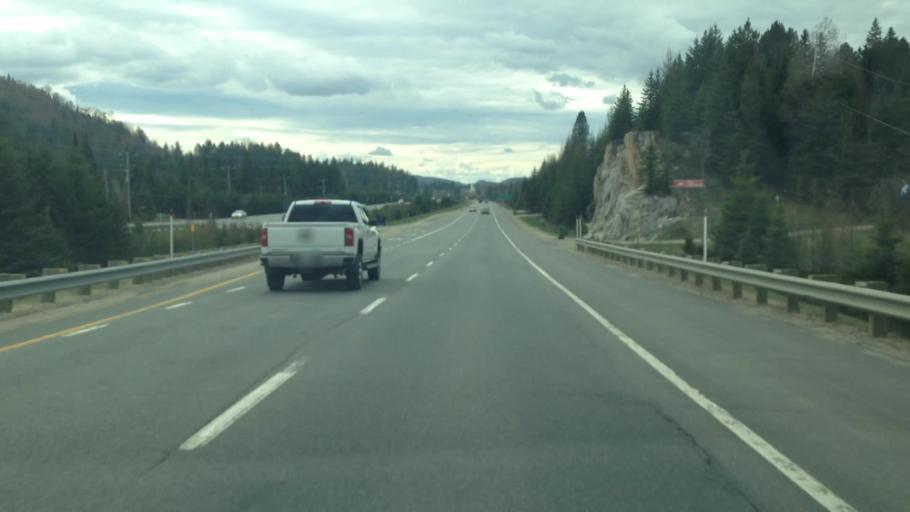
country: CA
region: Quebec
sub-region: Laurentides
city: Mont-Tremblant
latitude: 46.1134
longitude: -74.5407
